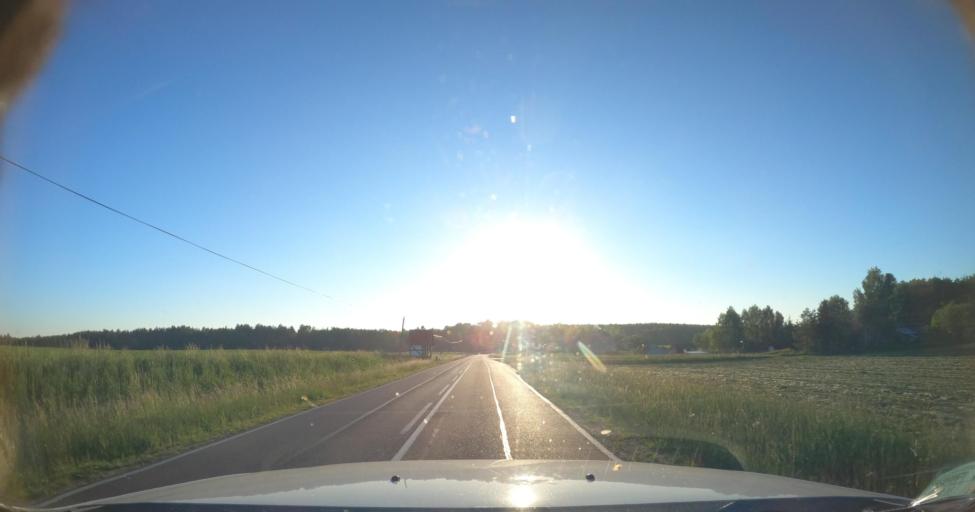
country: PL
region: Pomeranian Voivodeship
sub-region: Powiat bytowski
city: Czarna Dabrowka
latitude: 54.3659
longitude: 17.5078
